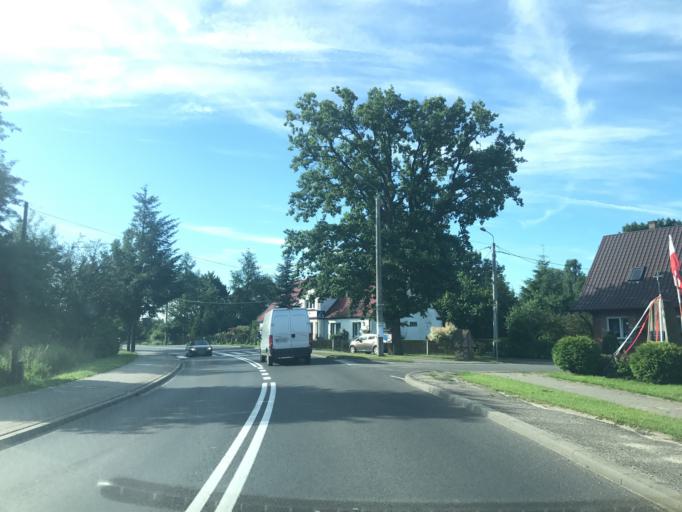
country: PL
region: Pomeranian Voivodeship
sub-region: Powiat czluchowski
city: Przechlewo
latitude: 53.7369
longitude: 17.1925
